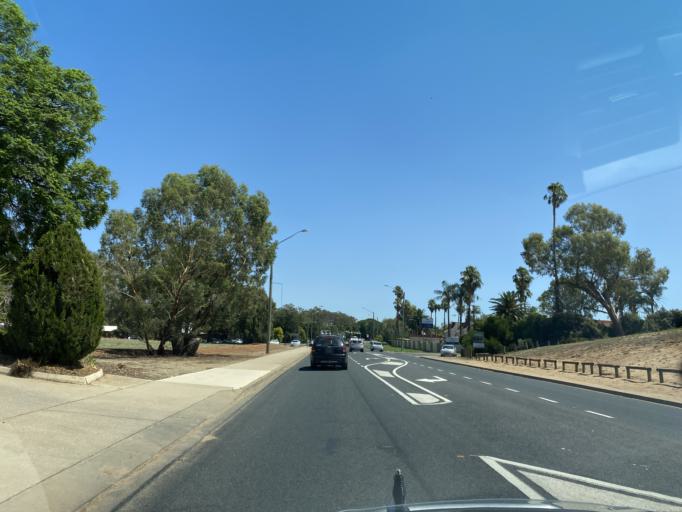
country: AU
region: New South Wales
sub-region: Corowa Shire
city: Mulwala
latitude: -36.0020
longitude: 146.0023
